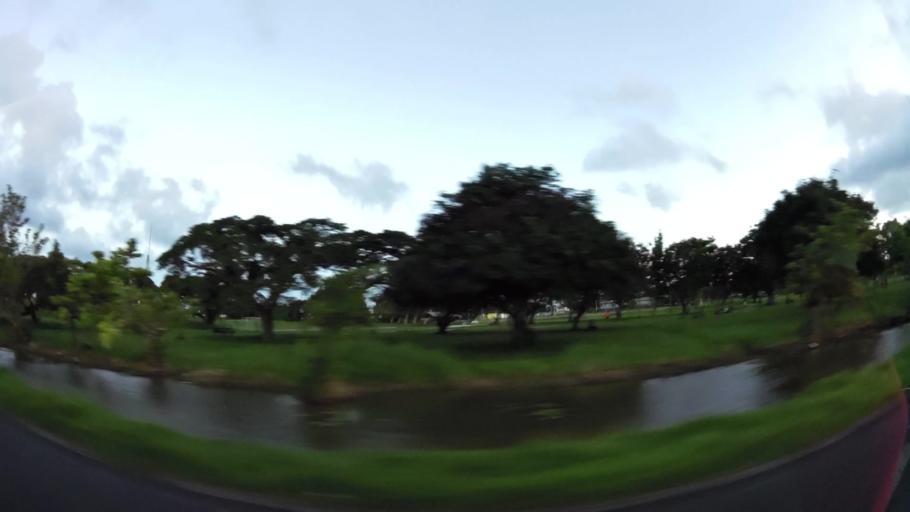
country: GY
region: Demerara-Mahaica
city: Georgetown
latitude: 6.8238
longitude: -58.1493
